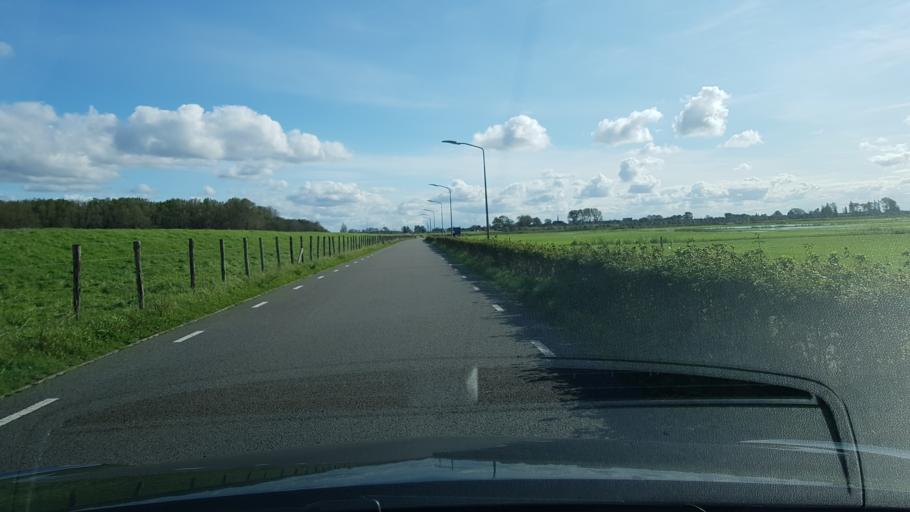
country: NL
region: North Holland
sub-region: Gemeente Velsen
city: Velsen-Zuid
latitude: 52.4229
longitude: 4.6671
